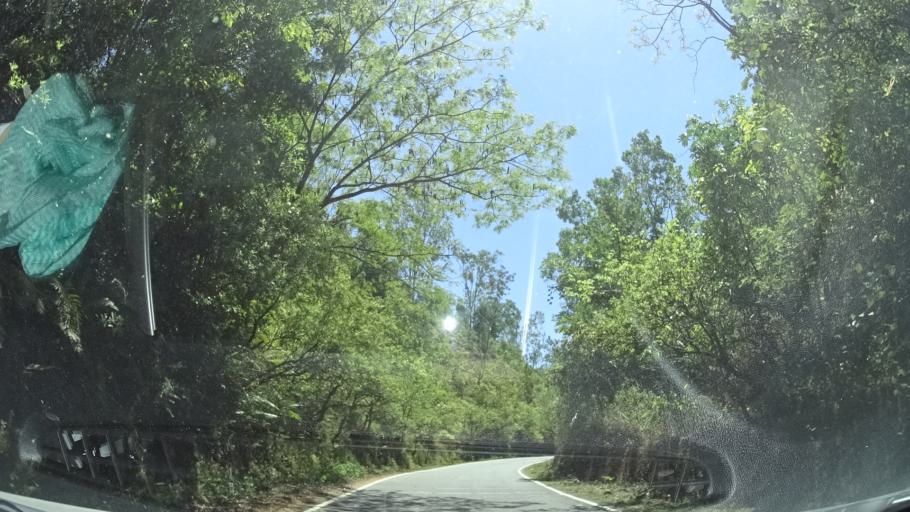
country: IN
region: Karnataka
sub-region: Chikmagalur
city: Sringeri
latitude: 13.2178
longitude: 75.2381
